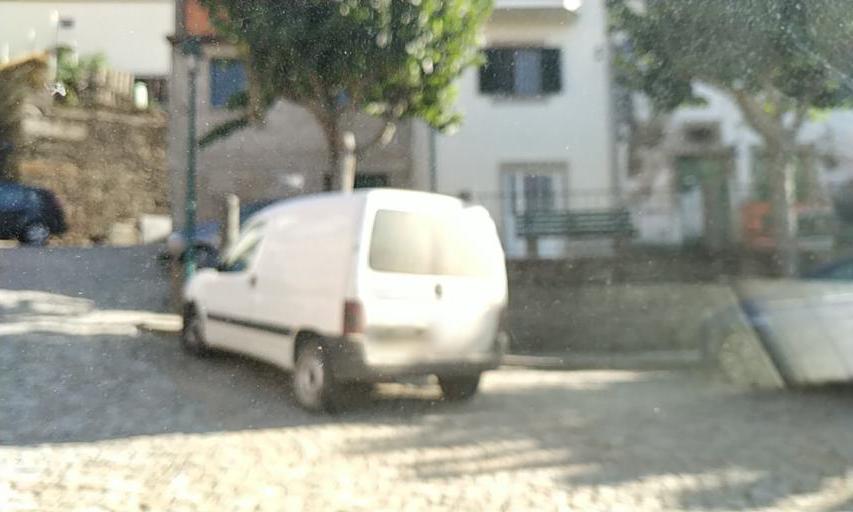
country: PT
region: Viseu
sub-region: Sao Joao da Pesqueira
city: Sao Joao da Pesqueira
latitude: 41.1869
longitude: -7.4329
